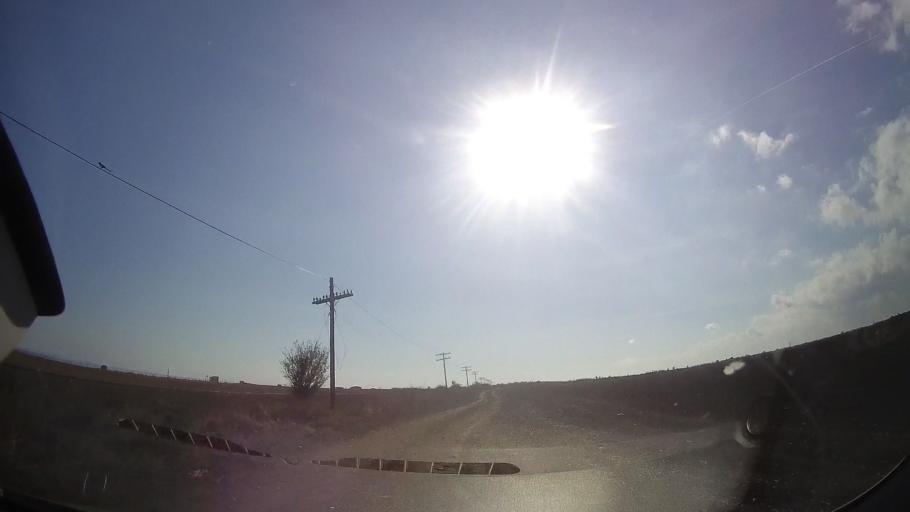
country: RO
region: Constanta
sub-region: Comuna Tuzla
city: Tuzla
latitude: 43.9803
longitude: 28.6443
